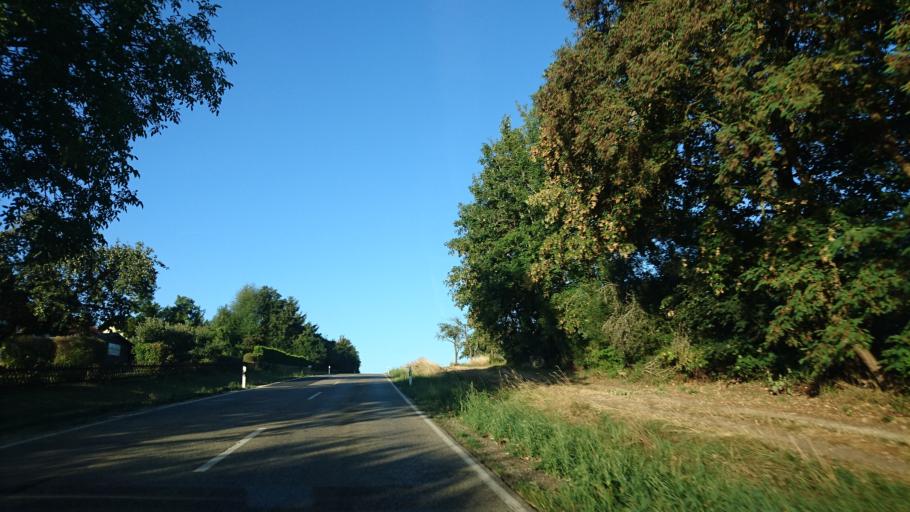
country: DE
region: Bavaria
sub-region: Regierungsbezirk Mittelfranken
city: Nennslingen
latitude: 49.0452
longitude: 11.1262
